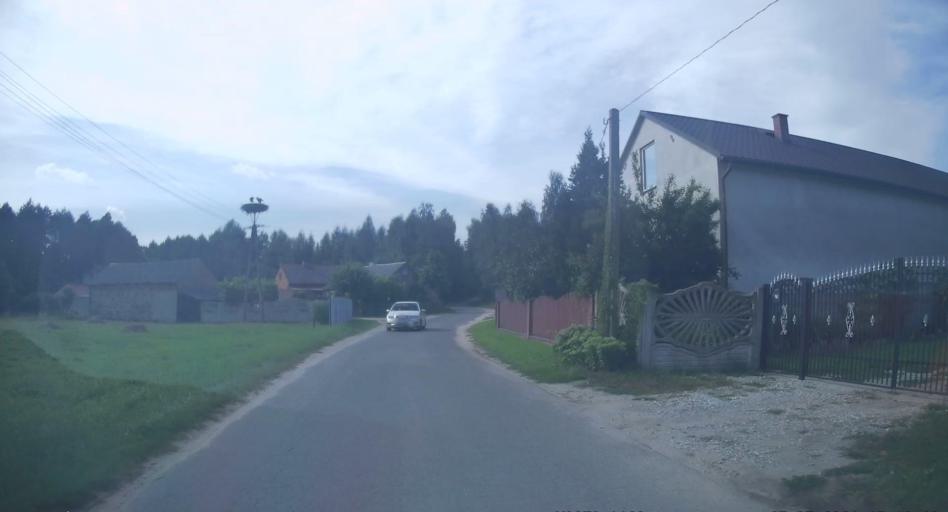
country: PL
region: Lodz Voivodeship
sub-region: Powiat rawski
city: Rawa Mazowiecka
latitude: 51.6945
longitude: 20.2520
